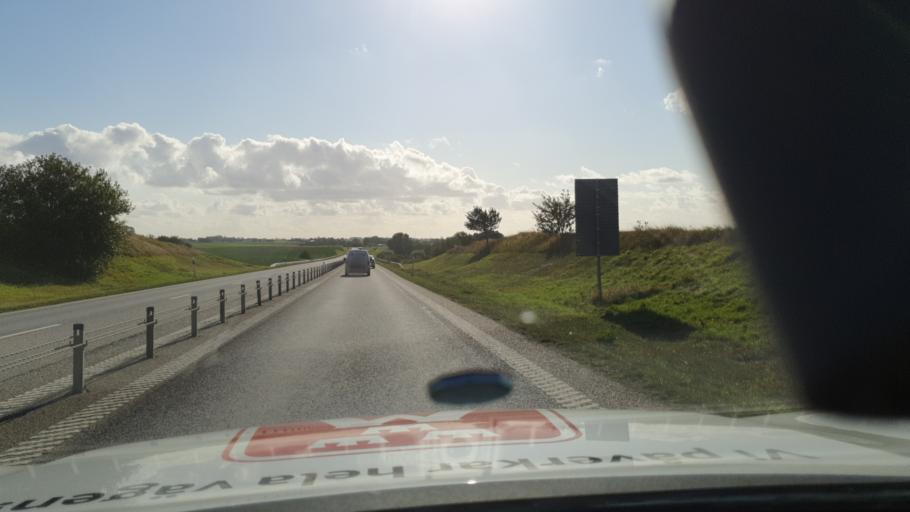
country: SE
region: Skane
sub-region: Svedala Kommun
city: Svedala
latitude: 55.4621
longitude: 13.1939
